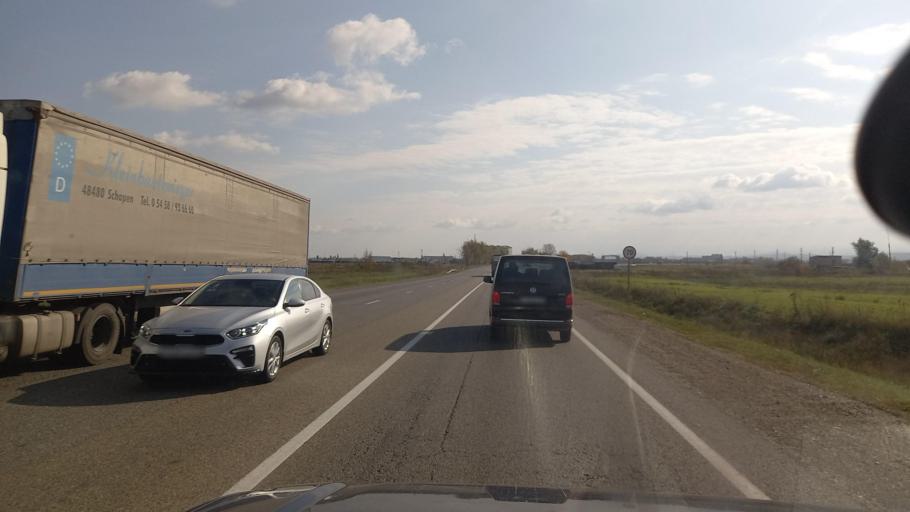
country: RU
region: Krasnodarskiy
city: Abinsk
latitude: 44.8728
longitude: 38.1201
